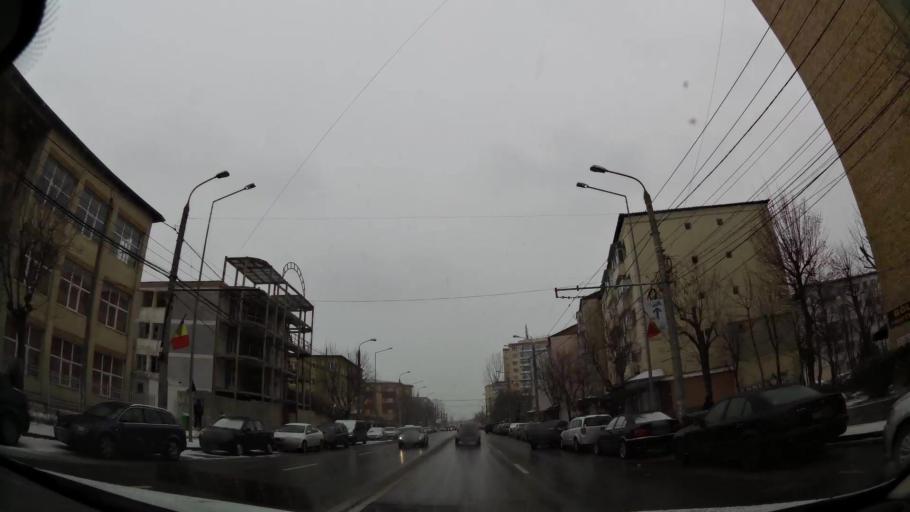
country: RO
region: Dambovita
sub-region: Municipiul Targoviste
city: Targoviste
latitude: 44.9222
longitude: 25.4461
